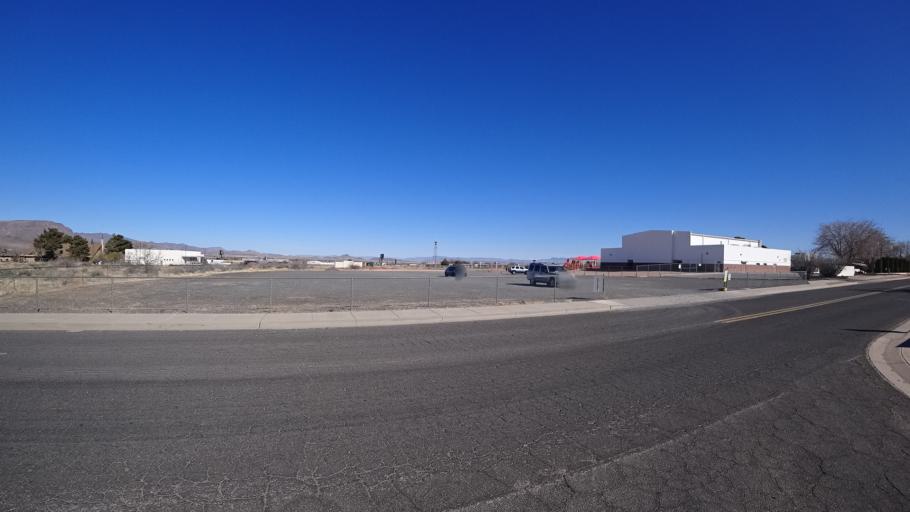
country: US
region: Arizona
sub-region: Mohave County
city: Kingman
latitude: 35.2139
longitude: -114.0190
